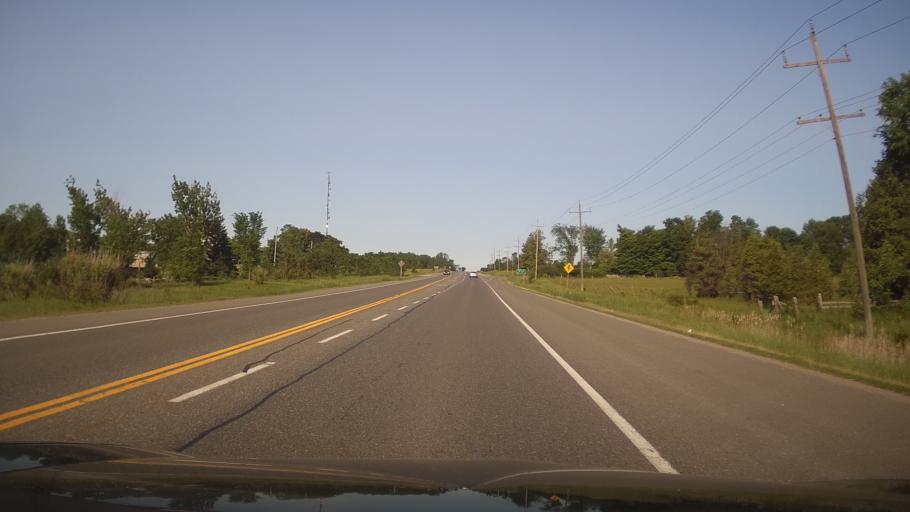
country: CA
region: Ontario
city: Peterborough
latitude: 44.3579
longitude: -78.0357
